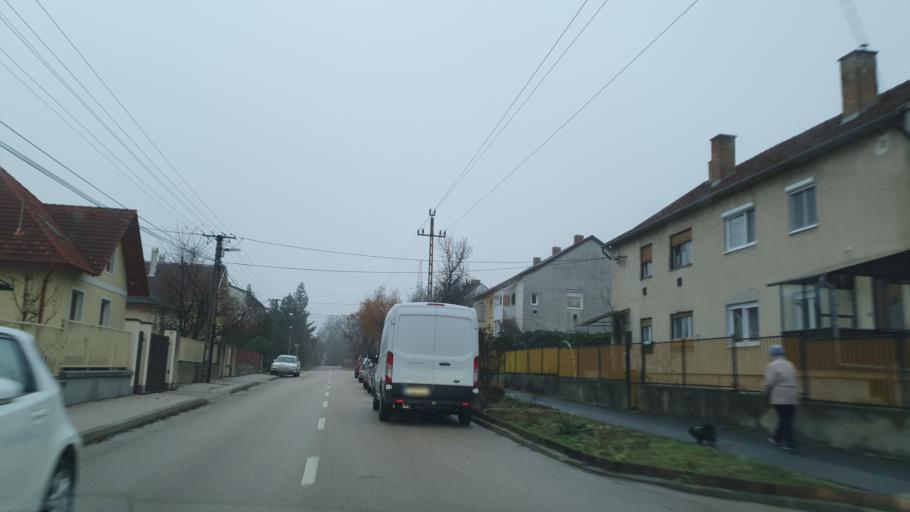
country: HU
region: Veszprem
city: Veszprem
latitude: 47.0801
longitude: 17.9109
